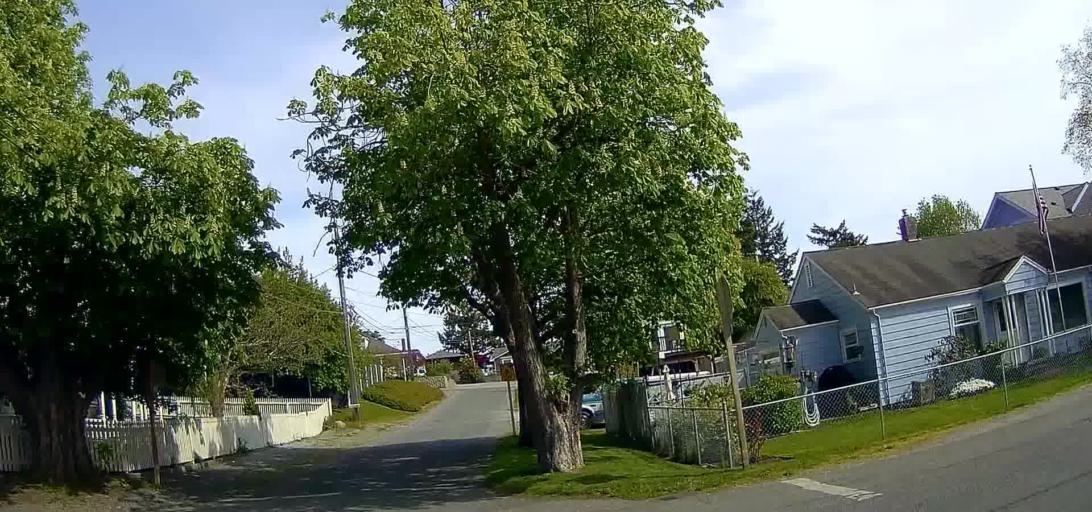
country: US
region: Washington
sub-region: Skagit County
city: Mount Vernon
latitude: 48.3899
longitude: -122.4957
